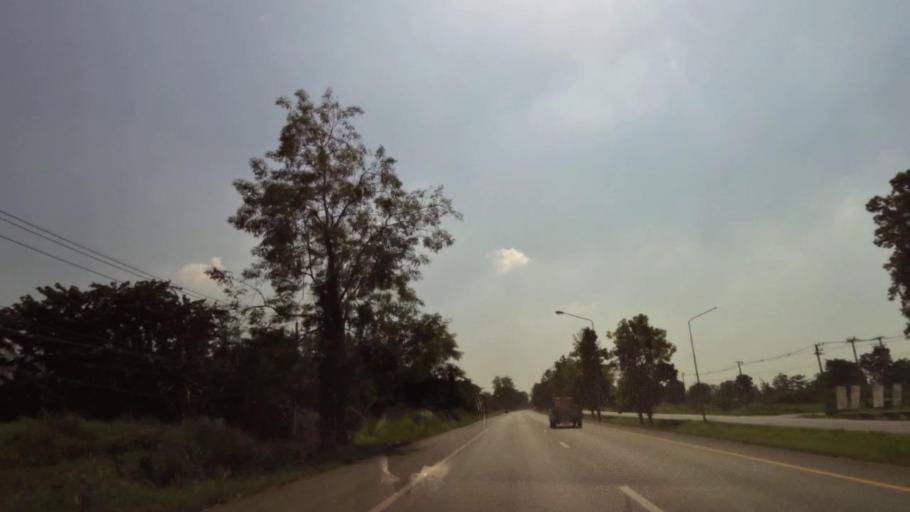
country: TH
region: Phichit
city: Bueng Na Rang
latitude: 16.1848
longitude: 100.1287
